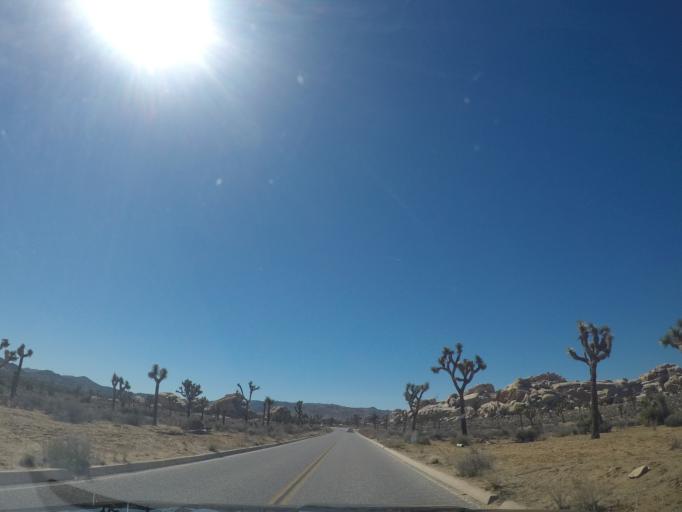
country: US
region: California
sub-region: San Bernardino County
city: Twentynine Palms
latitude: 34.0200
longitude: -116.1578
